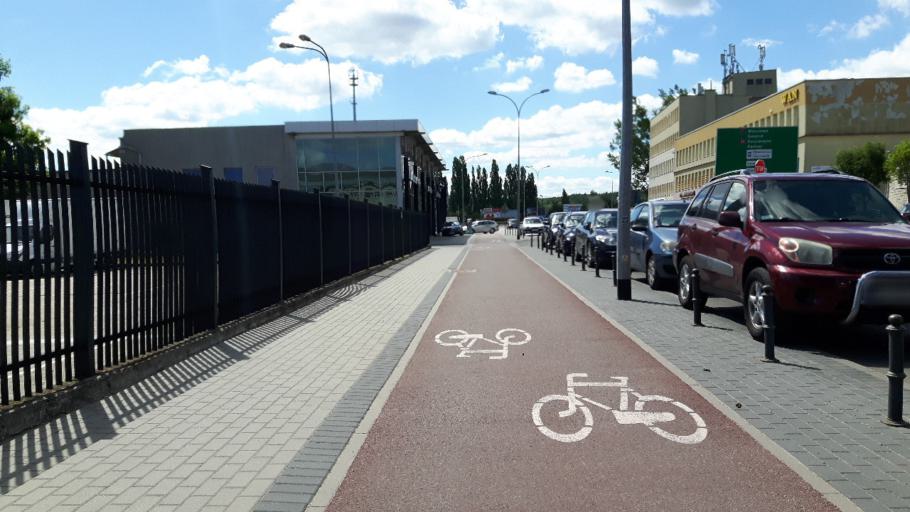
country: PL
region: Pomeranian Voivodeship
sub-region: Gdynia
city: Gdynia
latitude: 54.4929
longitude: 18.5350
